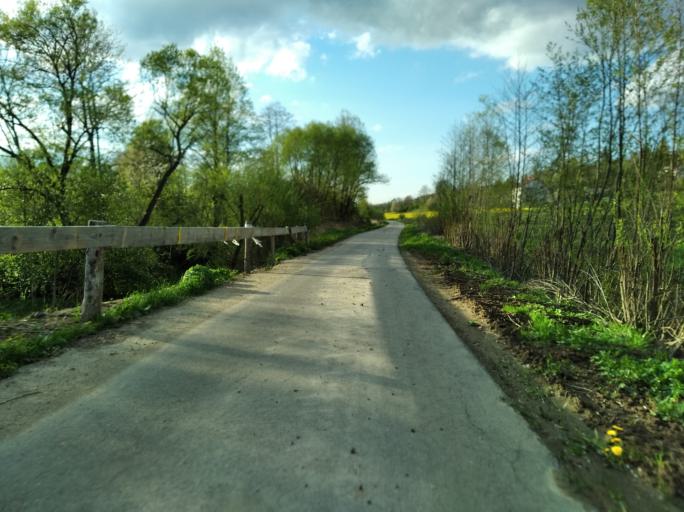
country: PL
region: Subcarpathian Voivodeship
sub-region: Powiat strzyzowski
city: Wysoka Strzyzowska
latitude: 49.8009
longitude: 21.7544
